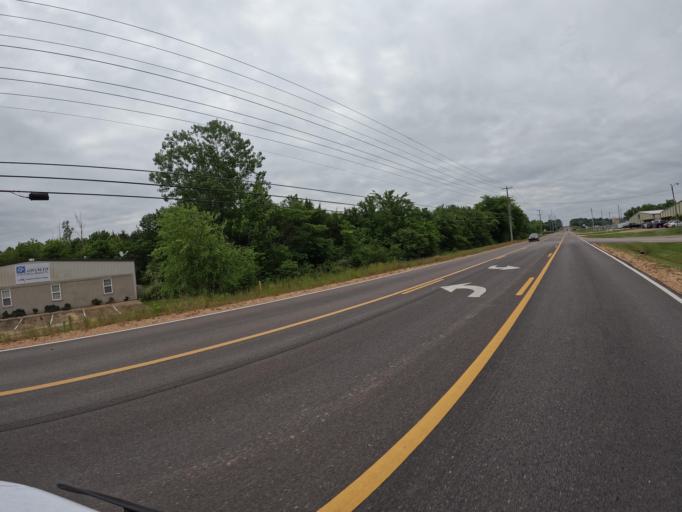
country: US
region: Mississippi
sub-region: Lee County
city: Tupelo
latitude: 34.2772
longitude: -88.7643
